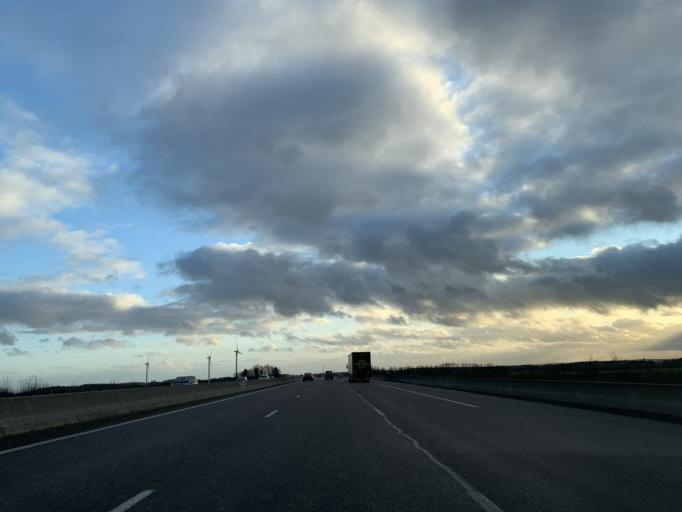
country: FR
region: Bourgogne
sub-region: Departement de la Cote-d'Or
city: Selongey
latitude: 47.7086
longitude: 5.1876
